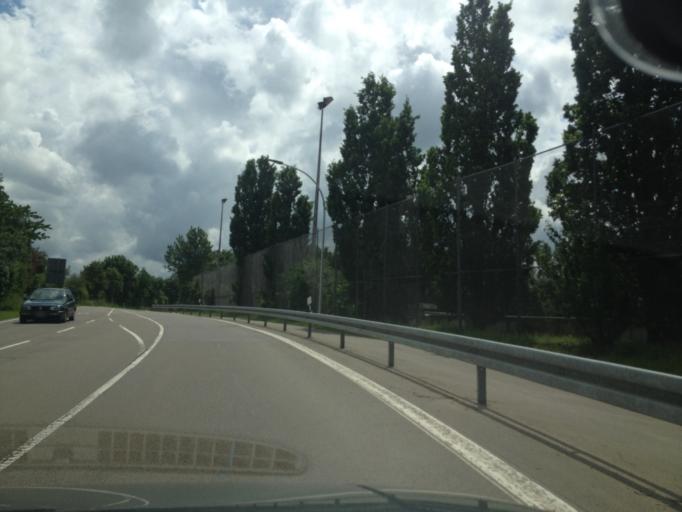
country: DE
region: Saarland
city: Bexbach
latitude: 49.3356
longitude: 7.2665
